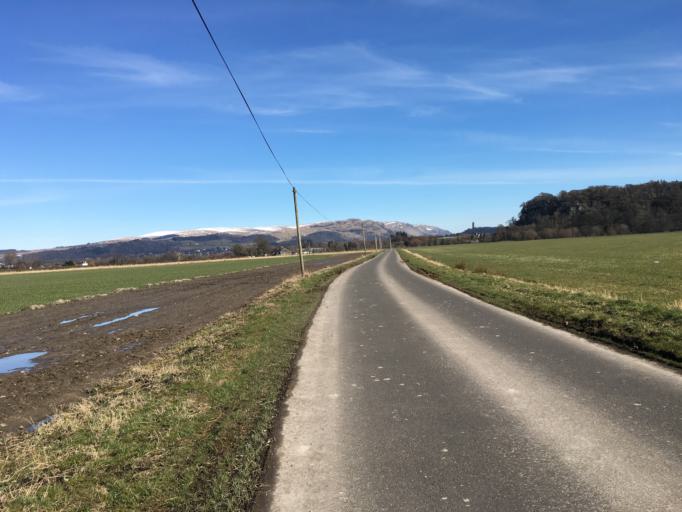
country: GB
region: Scotland
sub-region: Stirling
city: Bridge of Allan
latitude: 56.1310
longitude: -3.9912
